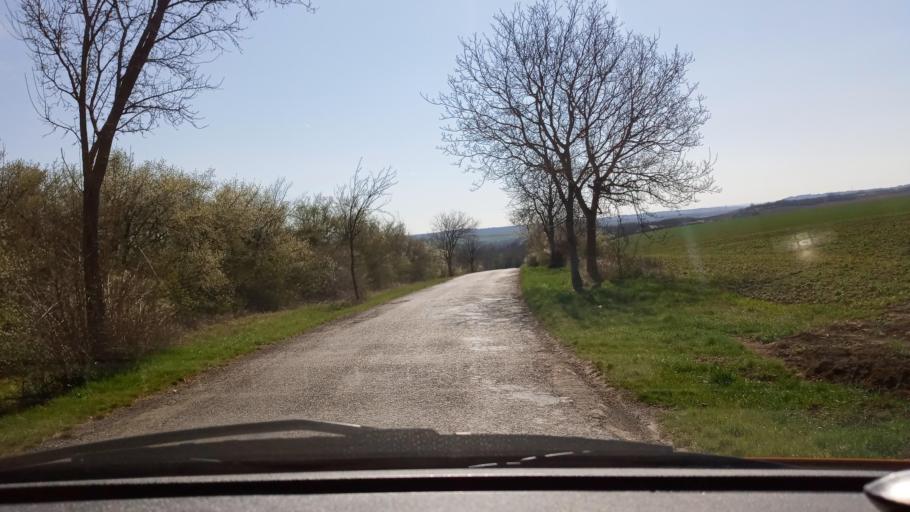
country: HU
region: Baranya
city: Kozarmisleny
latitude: 46.0753
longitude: 18.3549
